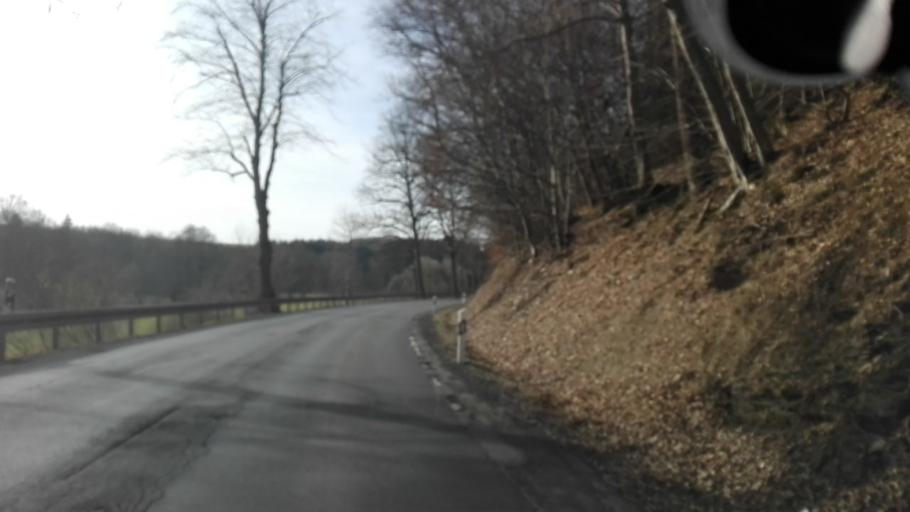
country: DE
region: North Rhine-Westphalia
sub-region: Regierungsbezirk Arnsberg
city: Bad Fredeburg
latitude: 51.1620
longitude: 8.3233
